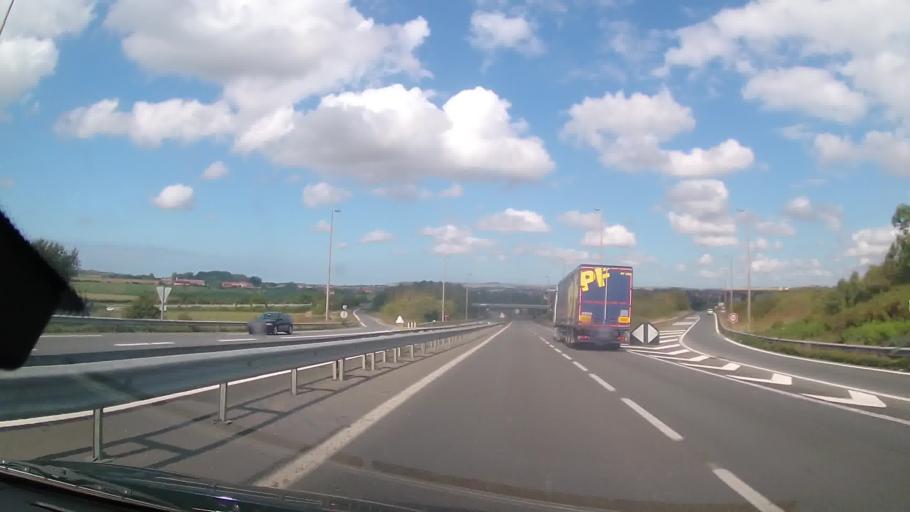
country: FR
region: Nord-Pas-de-Calais
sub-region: Departement du Pas-de-Calais
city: Marquise
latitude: 50.8049
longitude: 1.6924
